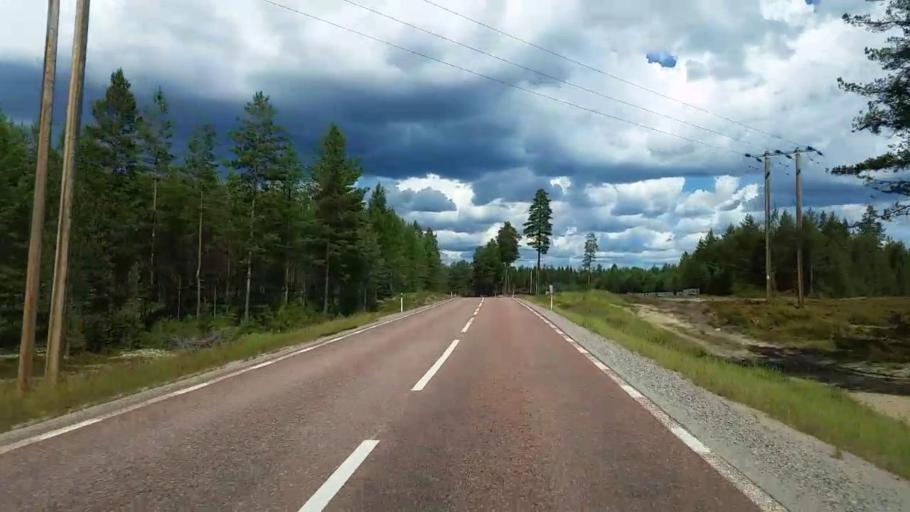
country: SE
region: Gaevleborg
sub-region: Ovanakers Kommun
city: Edsbyn
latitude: 61.3458
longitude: 15.5699
